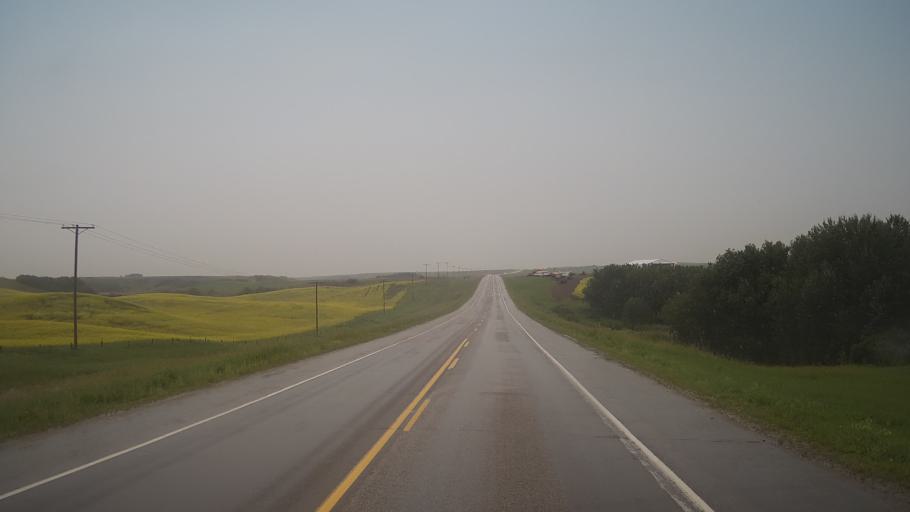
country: CA
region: Saskatchewan
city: Biggar
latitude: 52.0695
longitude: -108.0082
